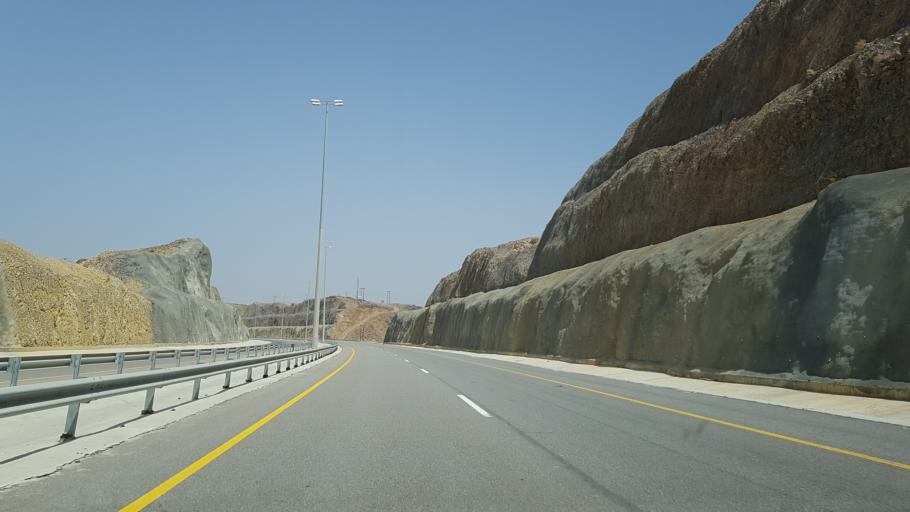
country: OM
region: Muhafazat Masqat
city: Muscat
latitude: 23.1887
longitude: 58.8563
